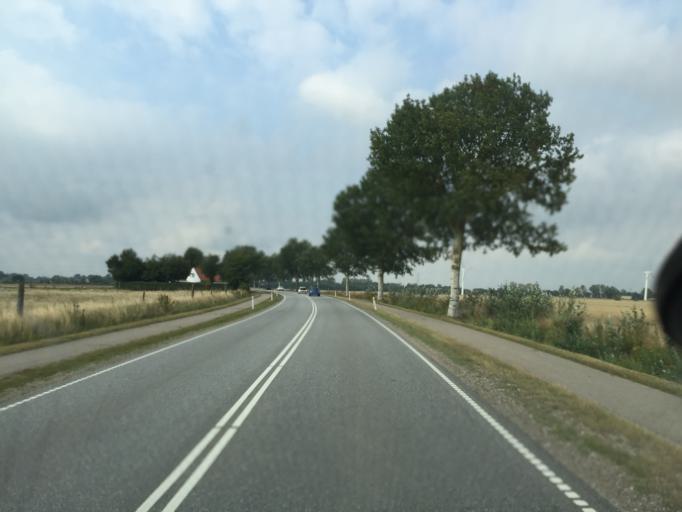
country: DK
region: Zealand
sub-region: Solrod Kommune
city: Solrod
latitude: 55.5391
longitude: 12.1769
